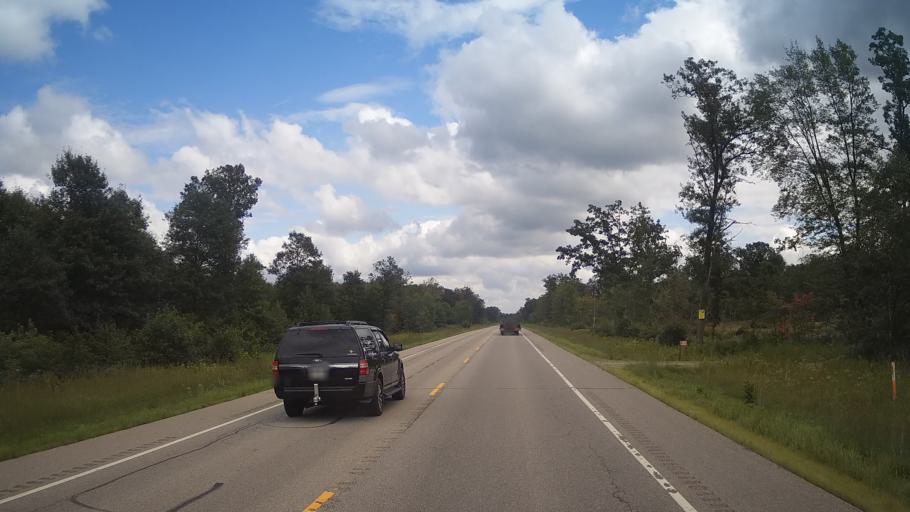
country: US
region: Wisconsin
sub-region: Adams County
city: Friendship
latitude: 44.0256
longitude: -89.7042
